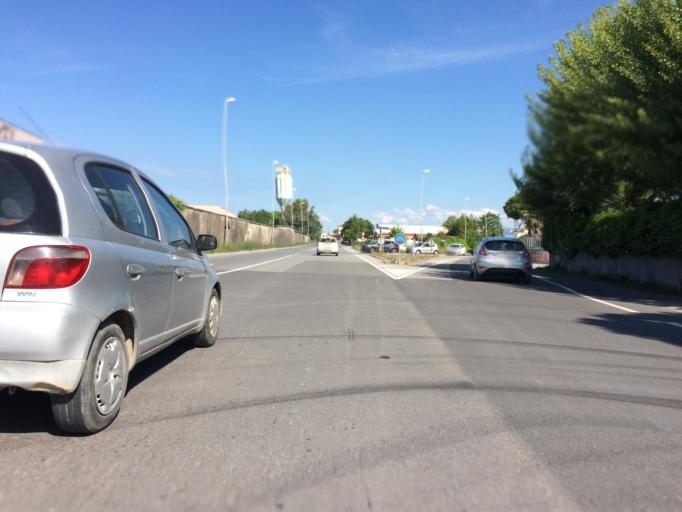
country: IT
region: Tuscany
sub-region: Provincia di Massa-Carrara
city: Carrara
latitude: 44.0406
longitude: 10.0683
